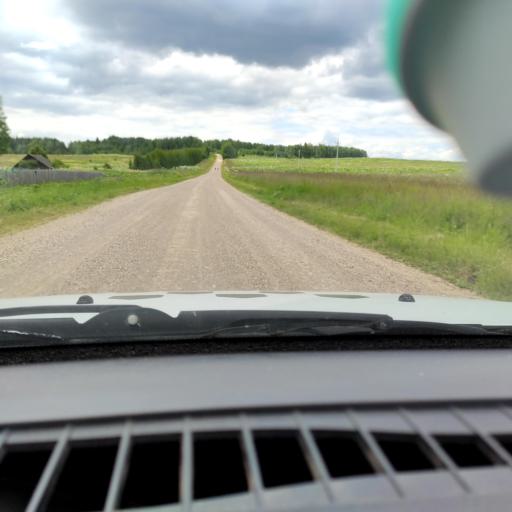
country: RU
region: Perm
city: Suksun
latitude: 57.2135
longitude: 57.6934
